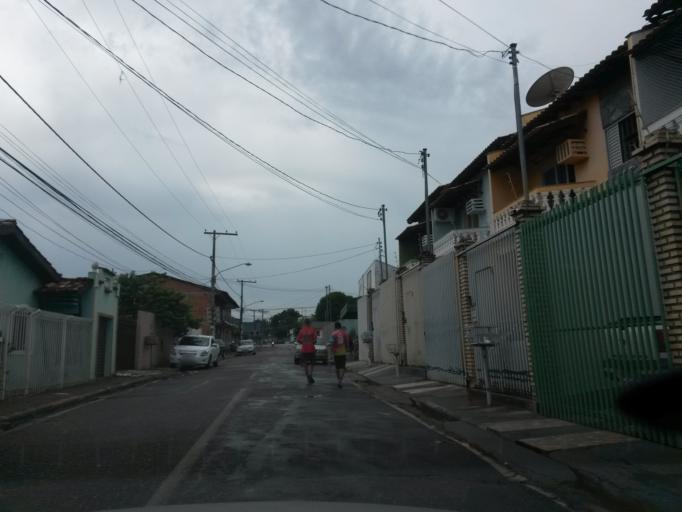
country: BR
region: Mato Grosso
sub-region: Cuiaba
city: Cuiaba
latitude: -15.6010
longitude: -56.0781
